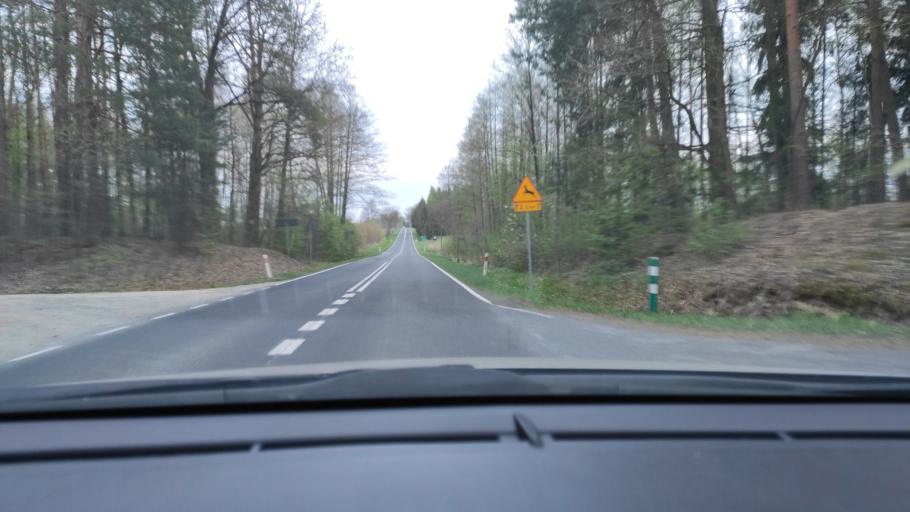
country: PL
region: Masovian Voivodeship
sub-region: Powiat zwolenski
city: Zwolen
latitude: 51.3874
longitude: 21.5528
